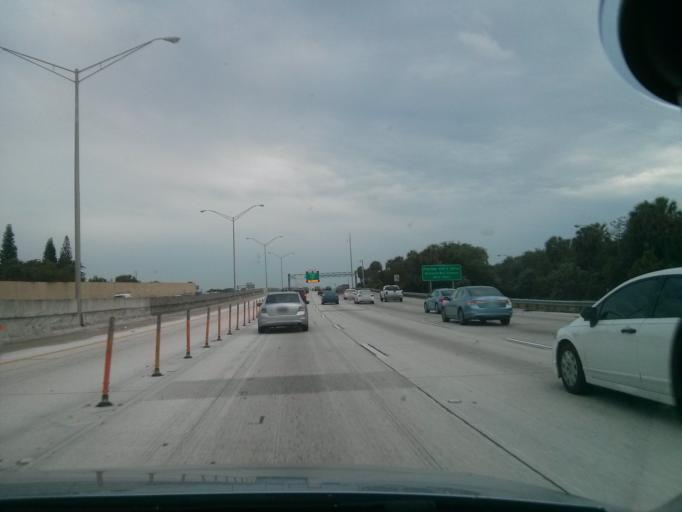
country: US
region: Florida
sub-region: Miami-Dade County
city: Golden Glades
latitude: 25.9154
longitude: -80.2103
